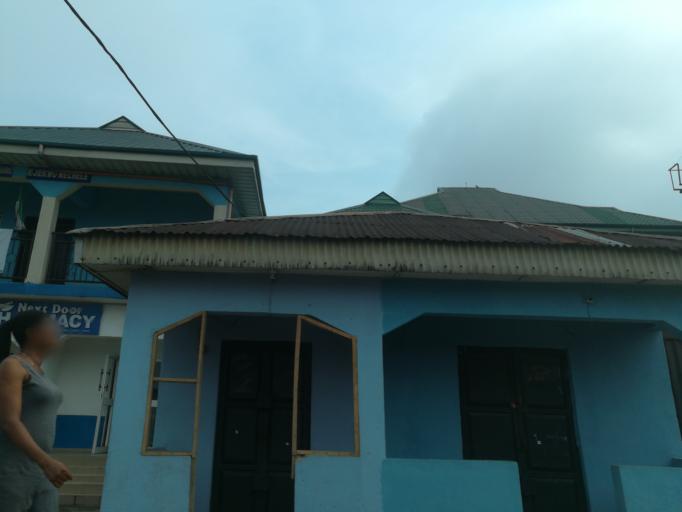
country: NG
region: Rivers
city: Port Harcourt
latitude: 4.8782
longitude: 6.9847
